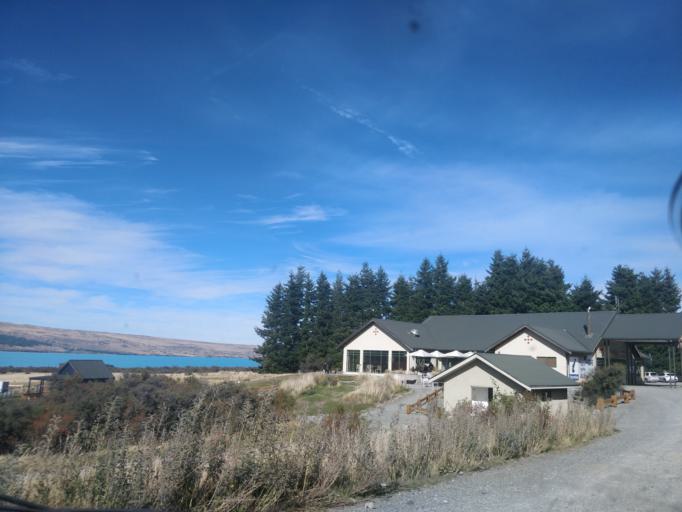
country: NZ
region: Canterbury
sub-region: Timaru District
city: Pleasant Point
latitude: -43.9113
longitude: 170.1211
